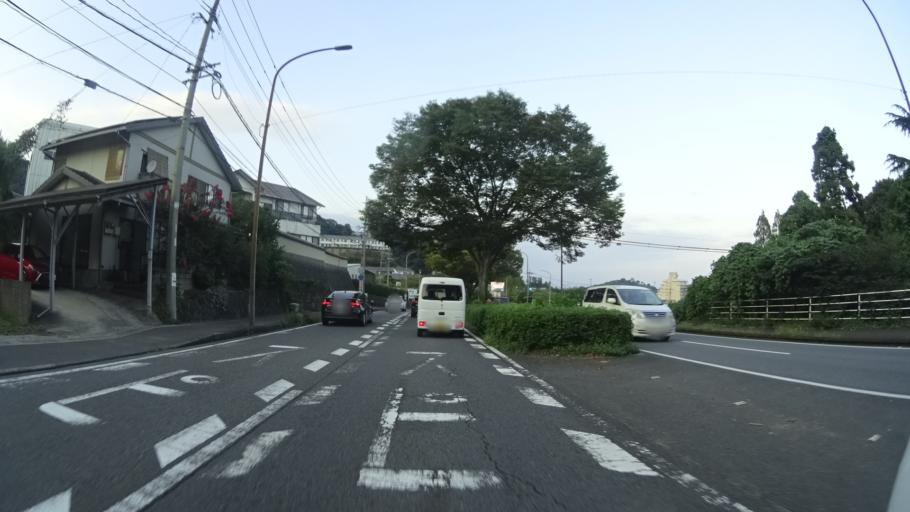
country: JP
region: Oita
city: Beppu
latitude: 33.3144
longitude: 131.4702
